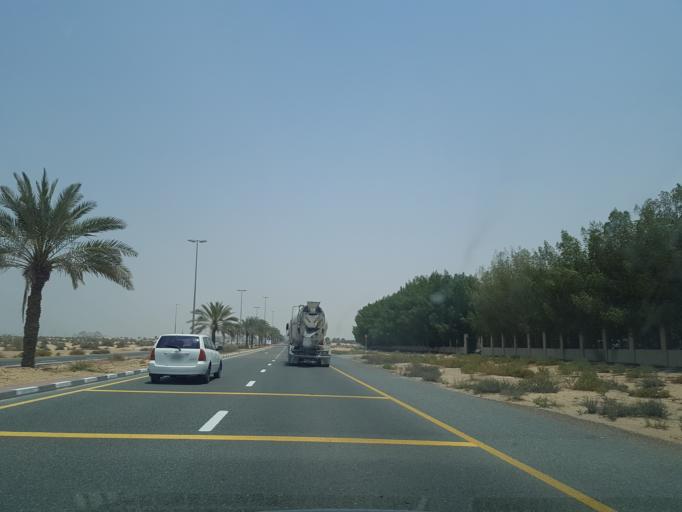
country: AE
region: Ash Shariqah
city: Sharjah
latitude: 25.1105
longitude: 55.4057
